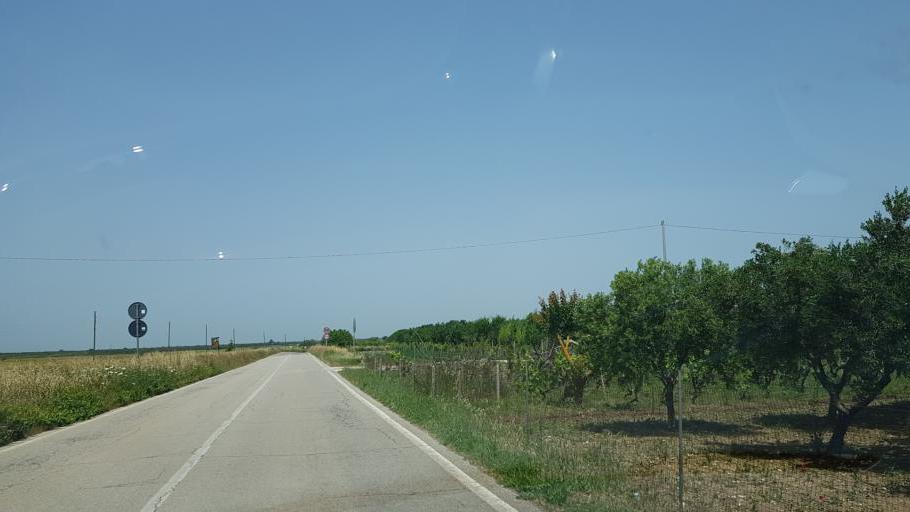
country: IT
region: Apulia
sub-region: Provincia di Brindisi
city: San Pancrazio Salentino
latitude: 40.4361
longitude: 17.8395
